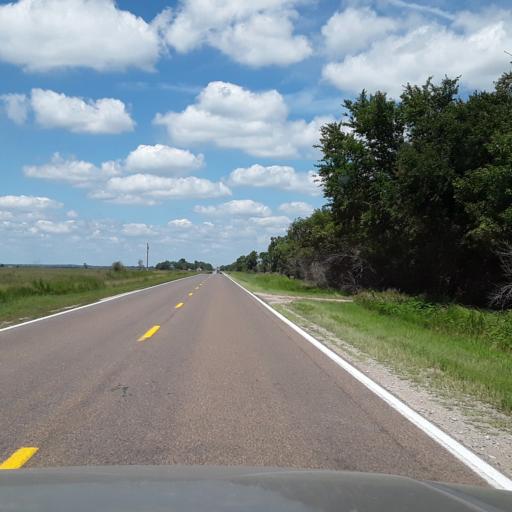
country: US
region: Nebraska
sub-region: Nance County
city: Genoa
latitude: 41.3566
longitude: -97.6949
